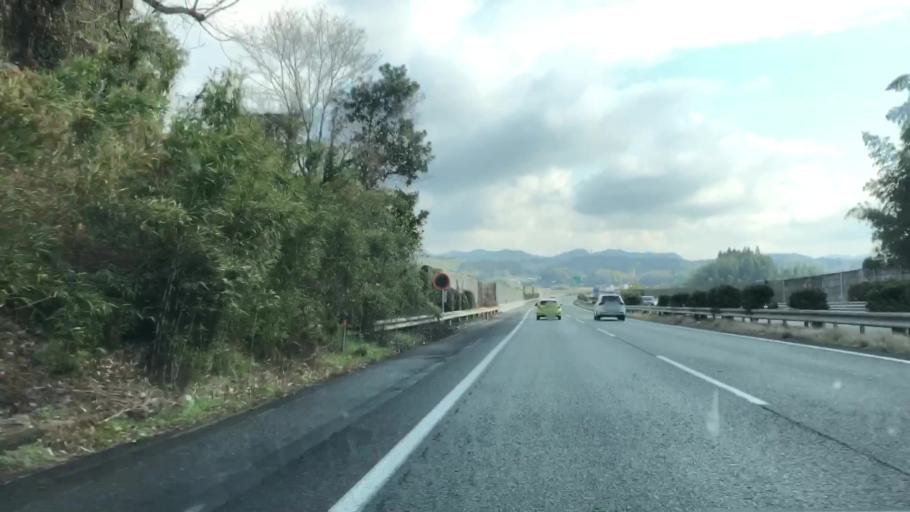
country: JP
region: Kumamoto
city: Tamana
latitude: 32.9971
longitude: 130.5950
